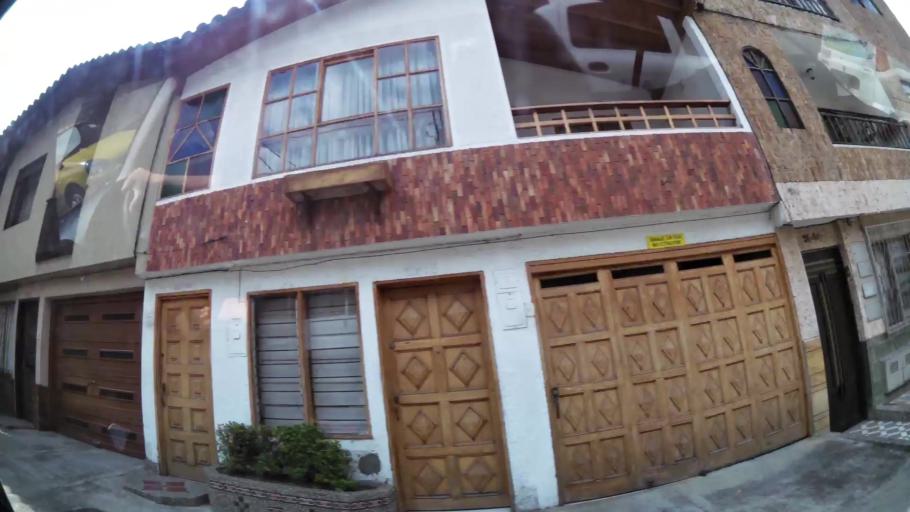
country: CO
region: Antioquia
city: Envigado
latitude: 6.1704
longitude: -75.5919
